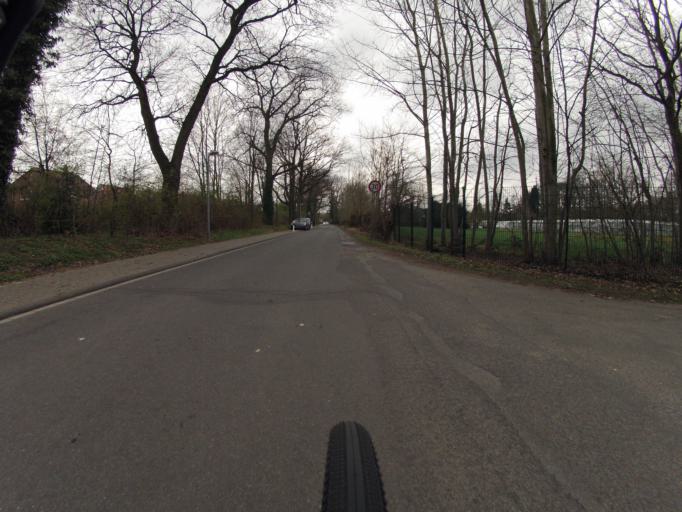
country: DE
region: North Rhine-Westphalia
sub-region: Regierungsbezirk Munster
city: Mettingen
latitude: 52.3239
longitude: 7.7692
